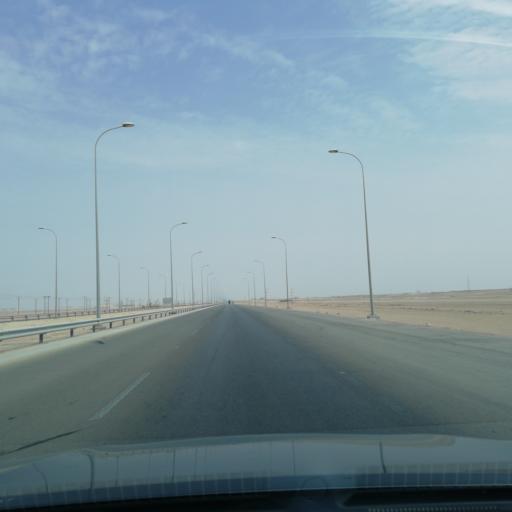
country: OM
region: Zufar
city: Salalah
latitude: 17.5761
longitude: 54.0444
